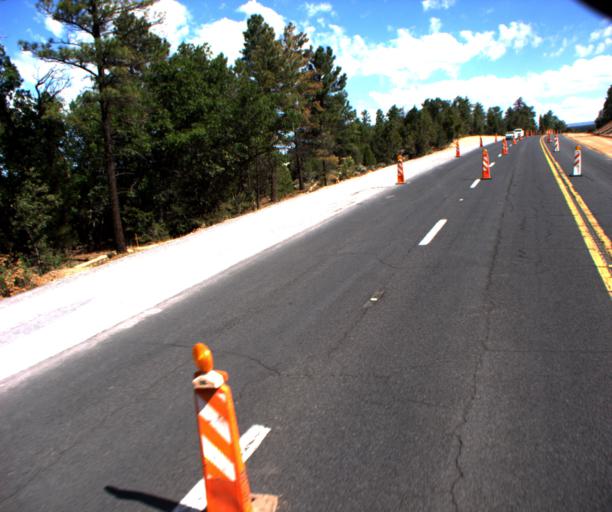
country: US
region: Arizona
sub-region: Coconino County
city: Grand Canyon Village
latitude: 35.9587
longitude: -112.1319
